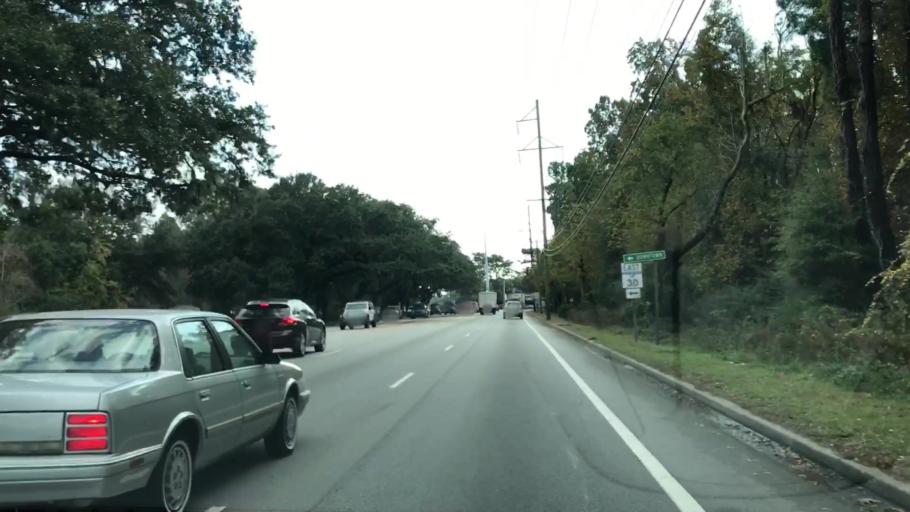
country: US
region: South Carolina
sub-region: Charleston County
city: Charleston
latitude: 32.7481
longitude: -79.9715
